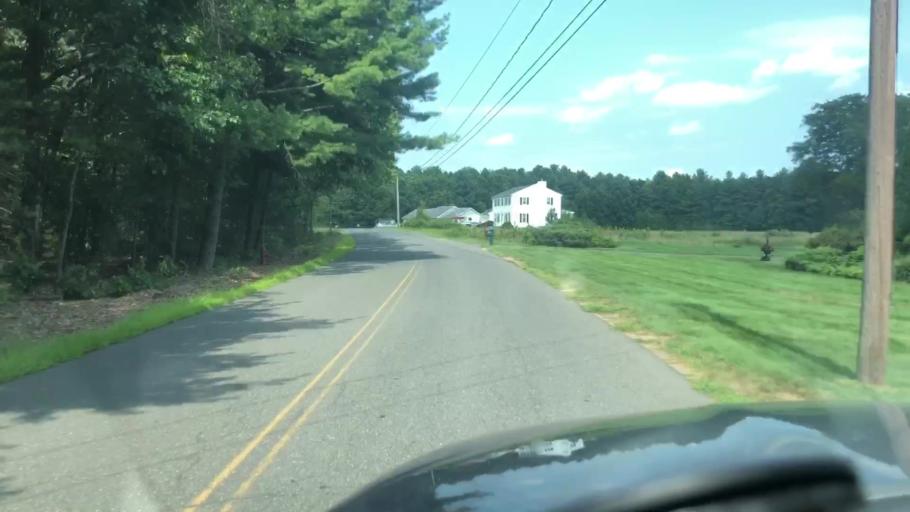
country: US
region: Massachusetts
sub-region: Hampshire County
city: Southampton
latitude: 42.1939
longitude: -72.6935
